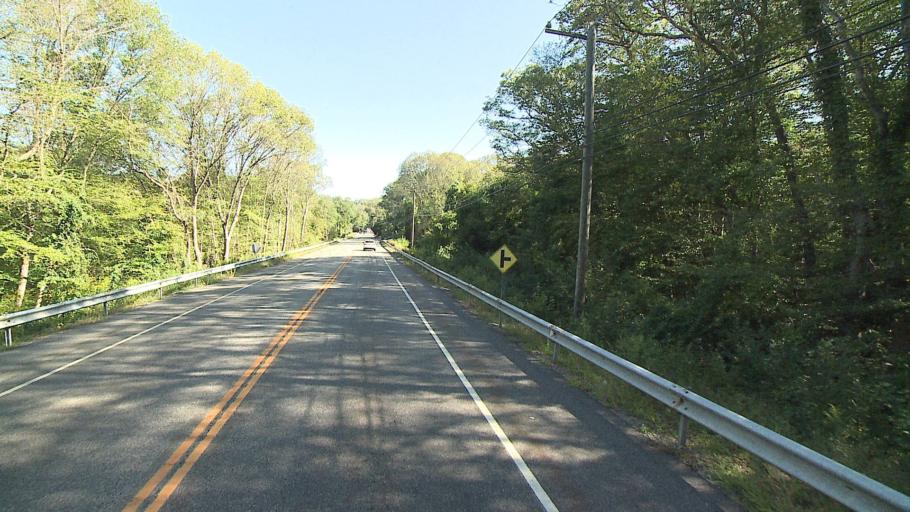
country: US
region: Connecticut
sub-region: New London County
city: Gales Ferry
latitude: 41.4642
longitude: -72.0602
